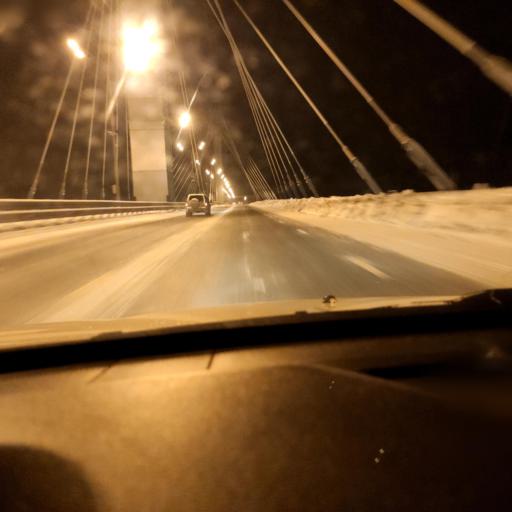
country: RU
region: Samara
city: Smyshlyayevka
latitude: 53.1806
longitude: 50.3063
